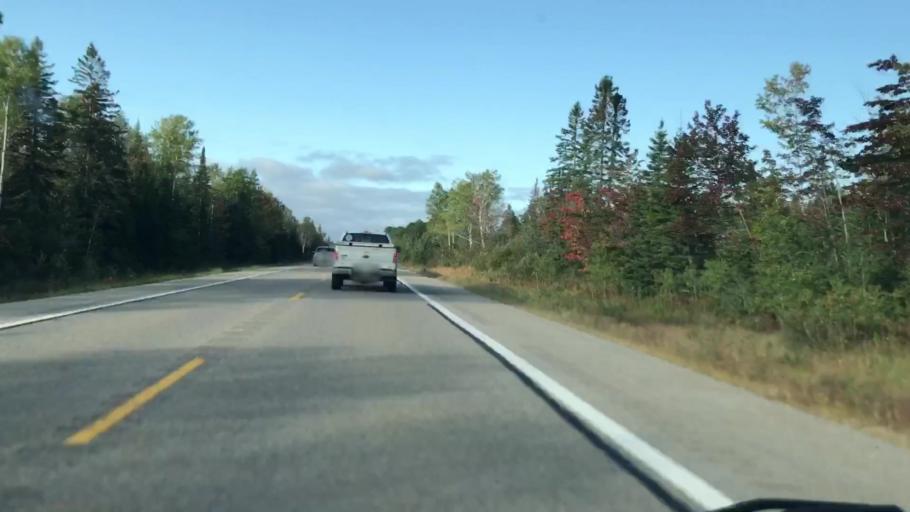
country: US
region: Michigan
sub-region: Luce County
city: Newberry
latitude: 46.3128
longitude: -85.2064
